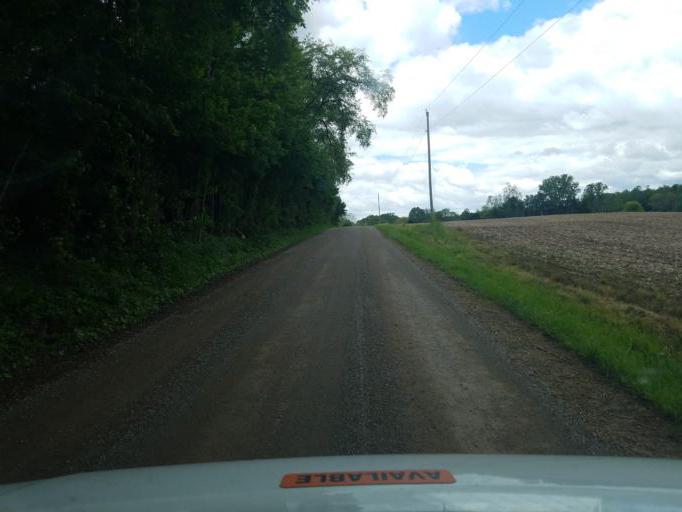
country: US
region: Ohio
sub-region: Richland County
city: Lexington
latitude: 40.6372
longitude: -82.6591
